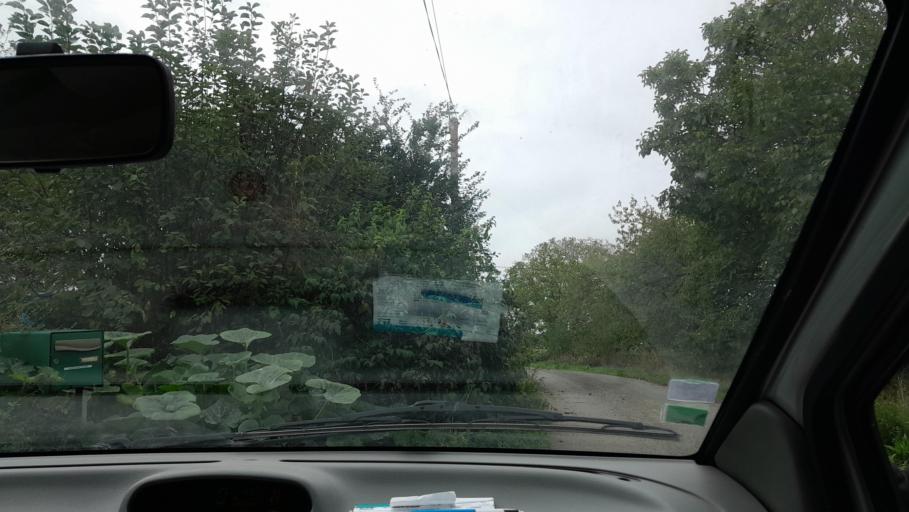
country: FR
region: Pays de la Loire
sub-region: Departement de la Mayenne
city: Ballots
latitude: 47.9592
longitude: -1.0607
